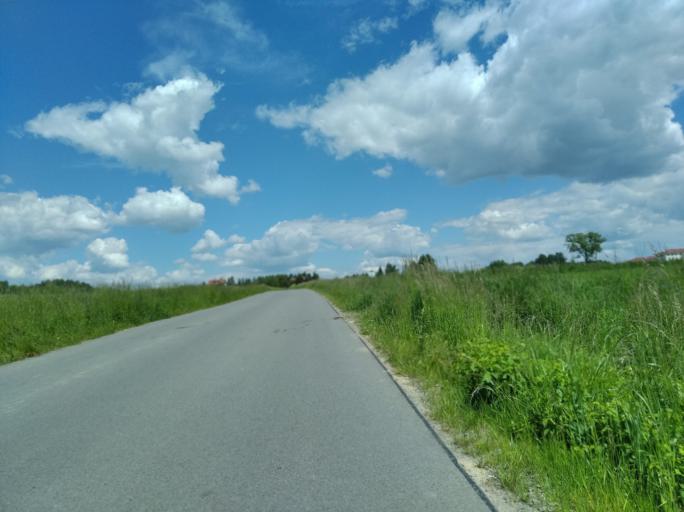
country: PL
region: Subcarpathian Voivodeship
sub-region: Powiat jasielski
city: Tarnowiec
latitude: 49.7722
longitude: 21.6114
